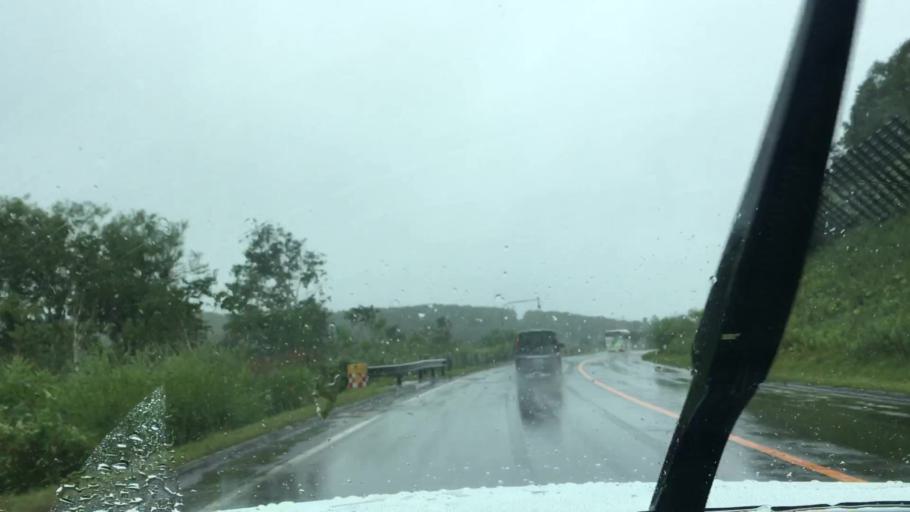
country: JP
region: Hokkaido
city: Sapporo
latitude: 42.8597
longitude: 141.1022
